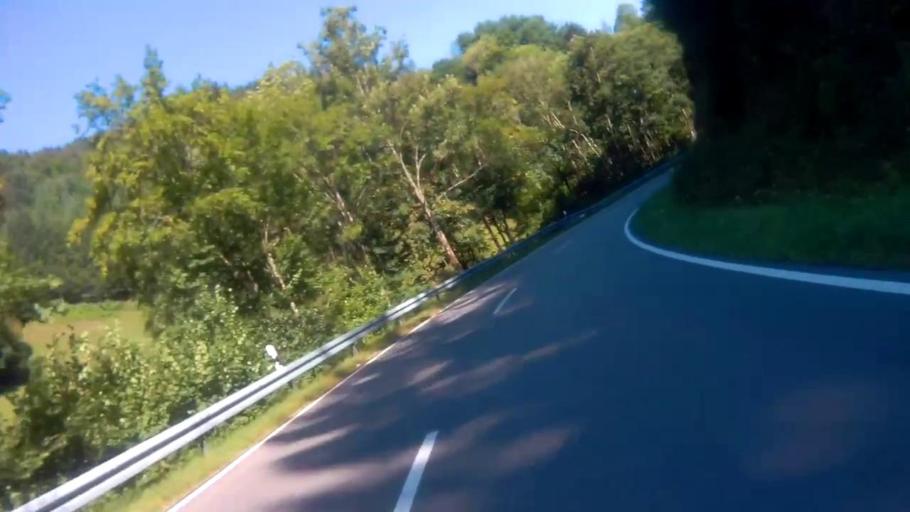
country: DE
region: Baden-Wuerttemberg
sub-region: Freiburg Region
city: Zell im Wiesental
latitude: 47.7430
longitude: 7.7657
